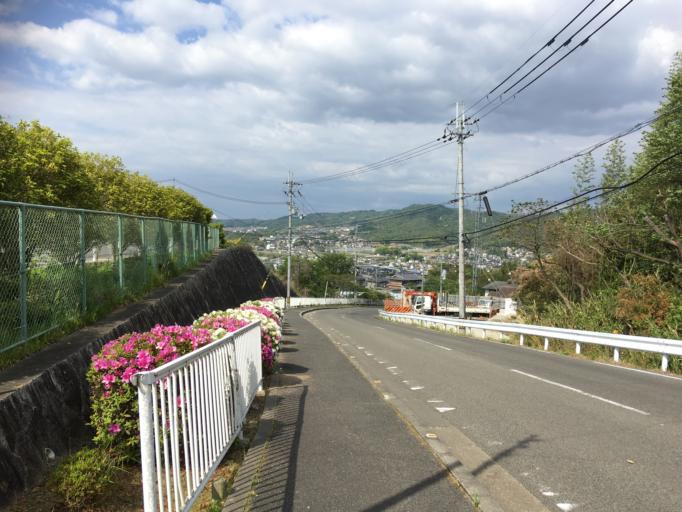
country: JP
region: Nara
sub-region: Ikoma-shi
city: Ikoma
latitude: 34.6258
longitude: 135.6907
